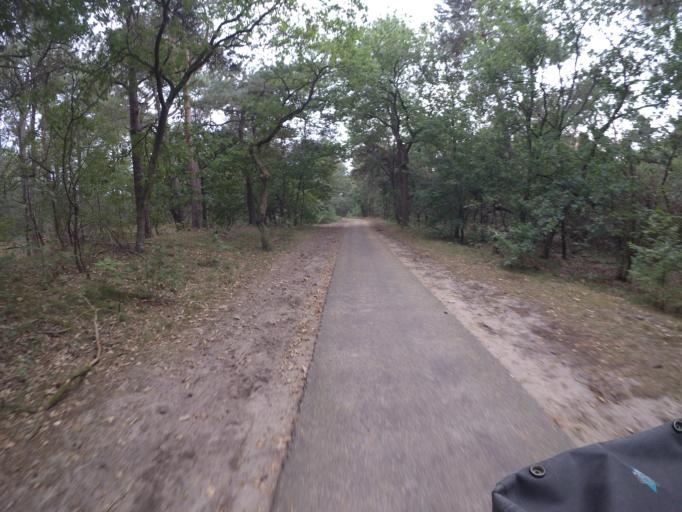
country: NL
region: North Brabant
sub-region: Gemeente Bernheze
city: Heesch
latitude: 51.7407
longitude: 5.5045
